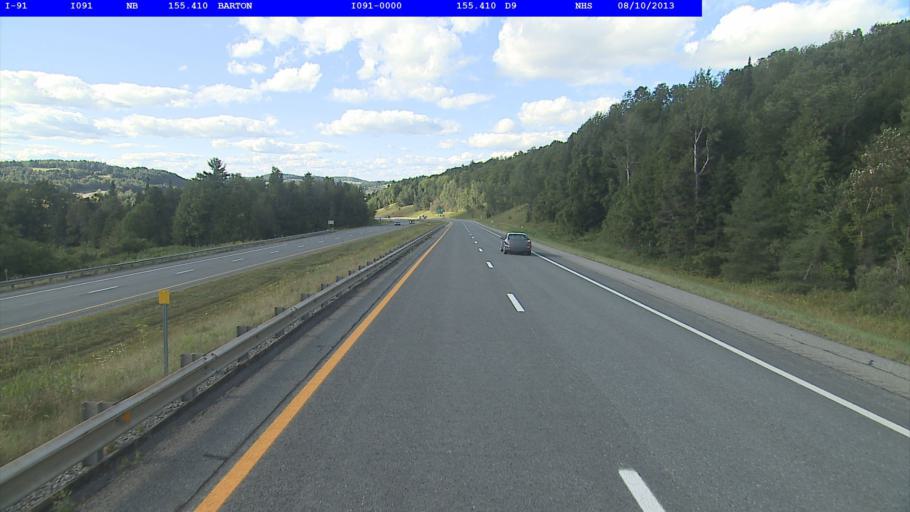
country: US
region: Vermont
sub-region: Orleans County
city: Newport
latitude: 44.7285
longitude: -72.1801
